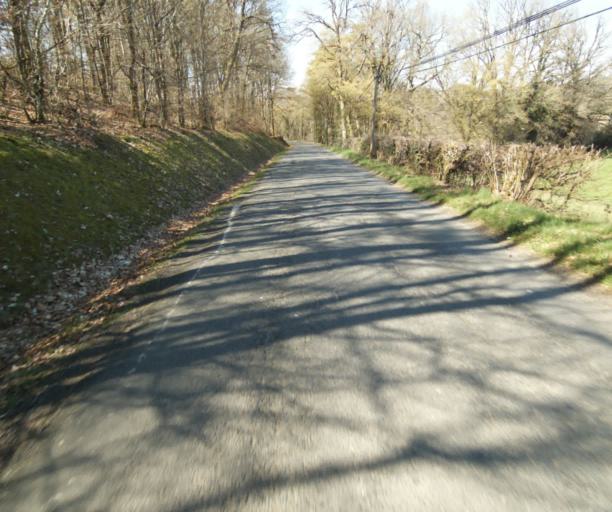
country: FR
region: Limousin
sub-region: Departement de la Correze
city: Saint-Mexant
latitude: 45.2980
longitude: 1.6805
